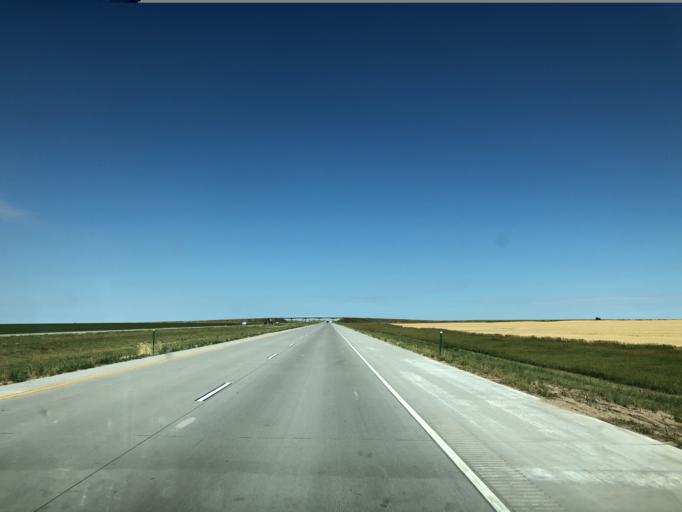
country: US
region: Colorado
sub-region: Kit Carson County
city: Burlington
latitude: 39.2942
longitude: -102.7716
